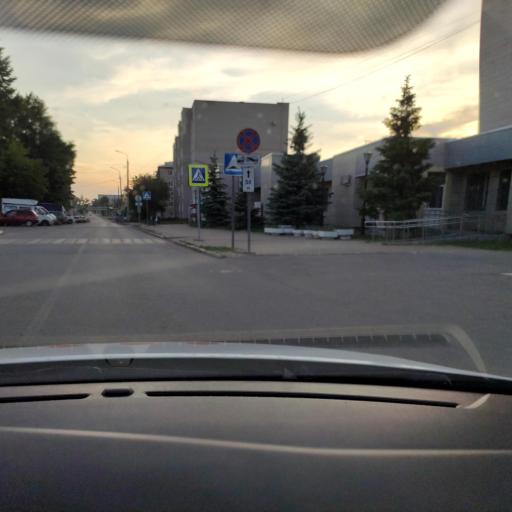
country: RU
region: Tatarstan
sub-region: Gorod Kazan'
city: Kazan
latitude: 55.7487
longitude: 49.1421
